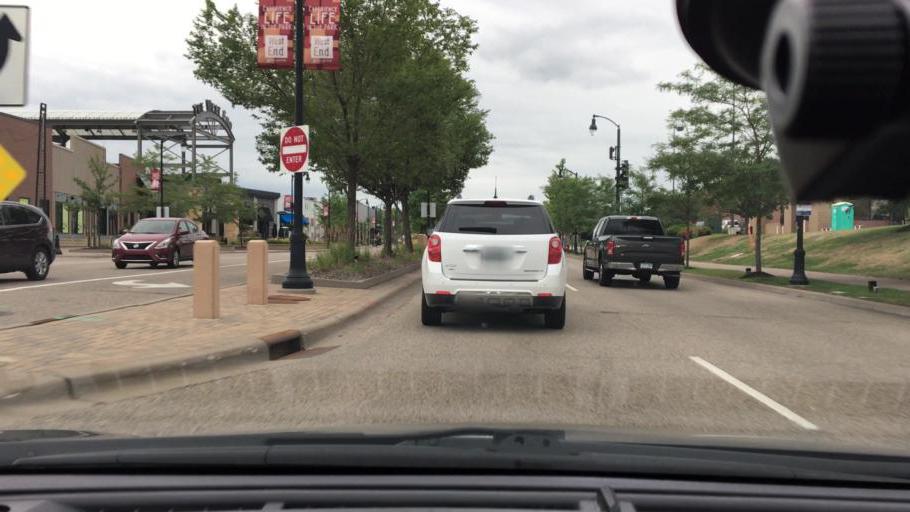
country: US
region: Minnesota
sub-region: Hennepin County
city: Saint Louis Park
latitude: 44.9675
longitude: -93.3495
